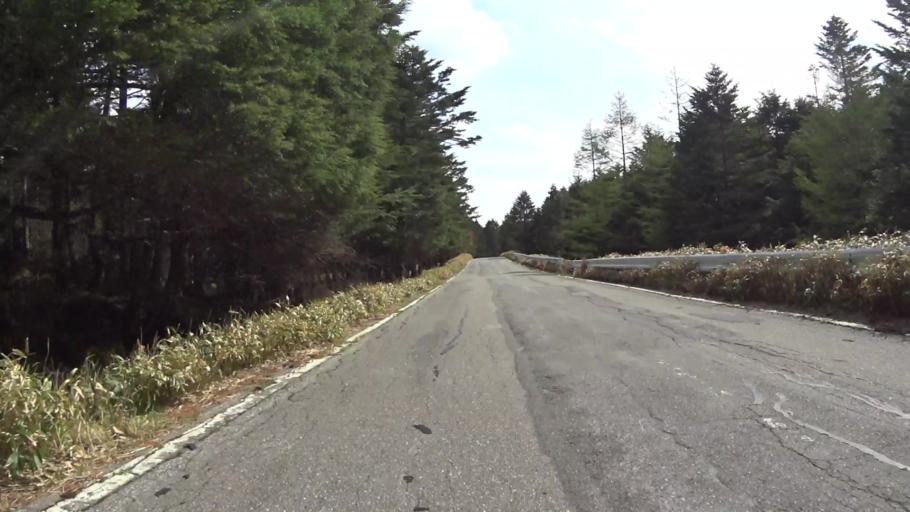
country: JP
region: Nagano
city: Chino
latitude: 36.0573
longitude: 138.3226
